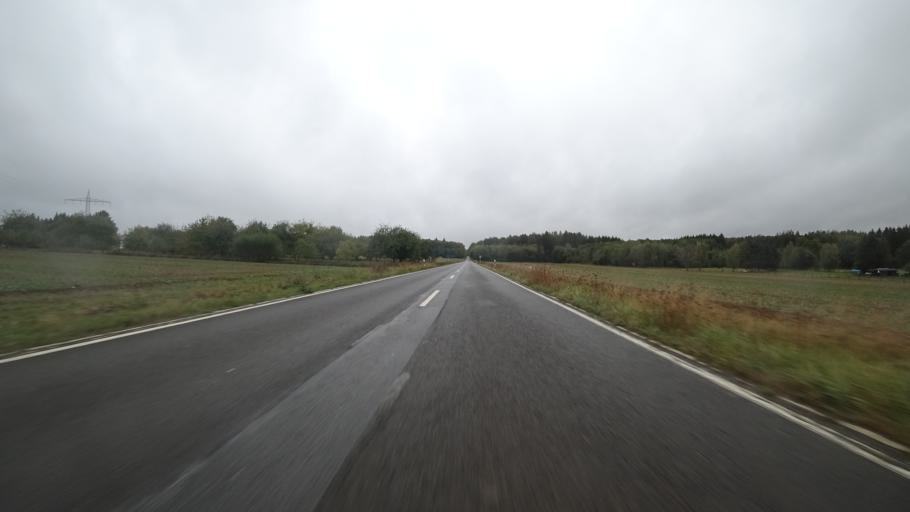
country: DE
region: Rheinland-Pfalz
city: Rheinbollen
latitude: 50.0086
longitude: 7.6552
